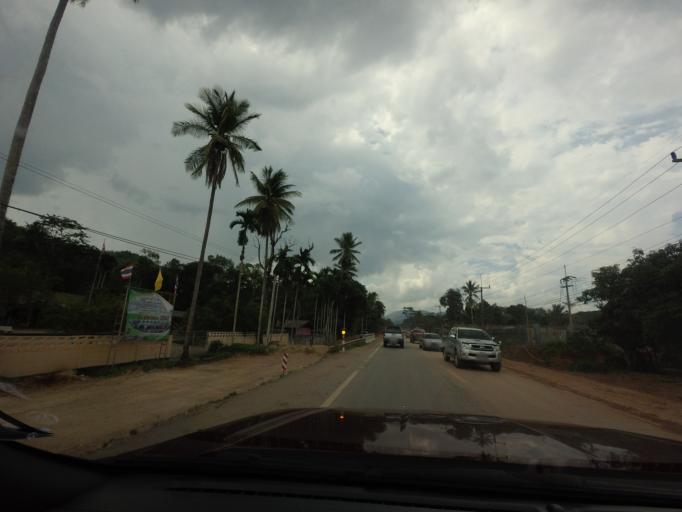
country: TH
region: Yala
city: Ban Nang Sata
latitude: 6.3177
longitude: 101.3035
